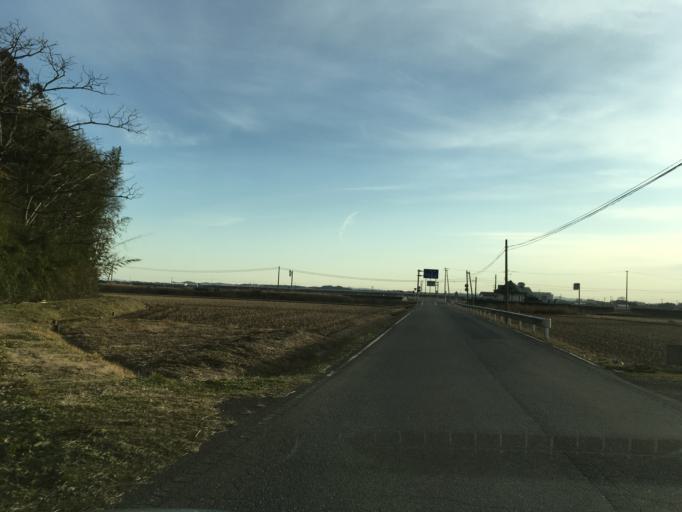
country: JP
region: Iwate
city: Ichinoseki
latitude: 38.7532
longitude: 141.1645
